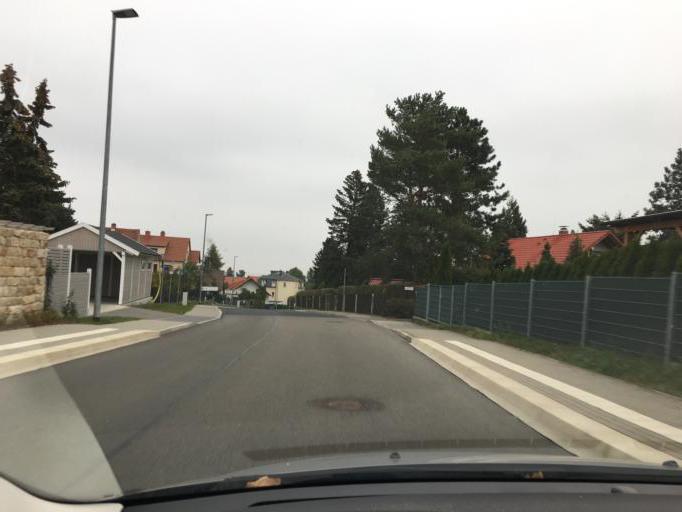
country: DE
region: Saxony
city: Freital
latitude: 51.0008
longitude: 13.6832
